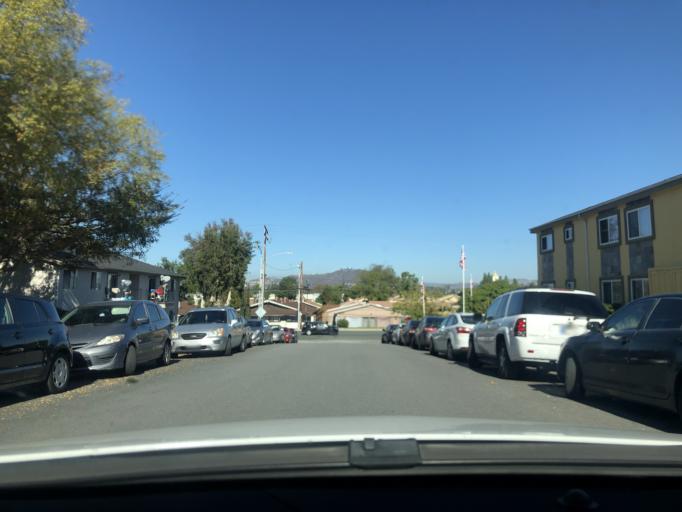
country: US
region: California
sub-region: San Diego County
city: Bostonia
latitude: 32.7869
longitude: -116.9425
